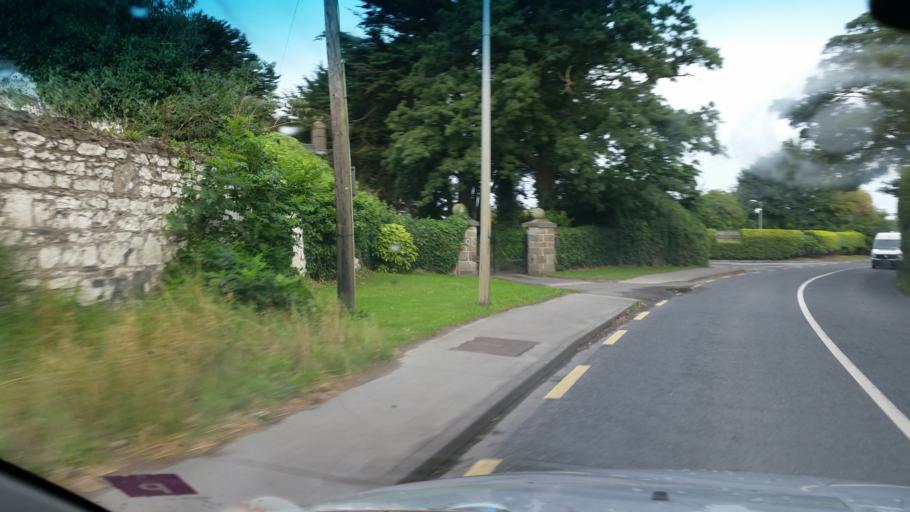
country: IE
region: Leinster
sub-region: Dublin City
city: Finglas
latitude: 53.4105
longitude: -6.3063
